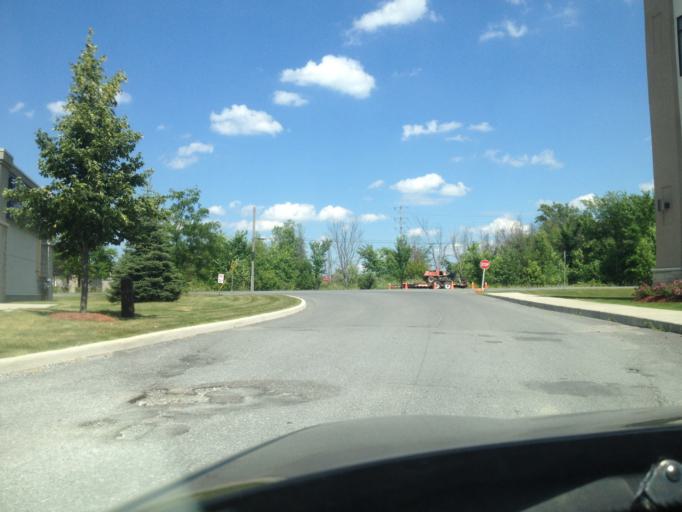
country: CA
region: Ontario
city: Bells Corners
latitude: 45.3071
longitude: -75.9163
